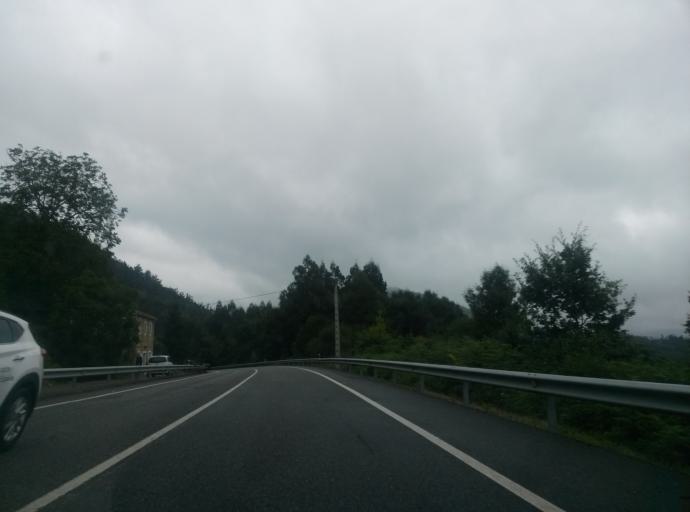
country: ES
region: Galicia
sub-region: Provincia de Lugo
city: Viveiro
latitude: 43.5776
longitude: -7.6339
